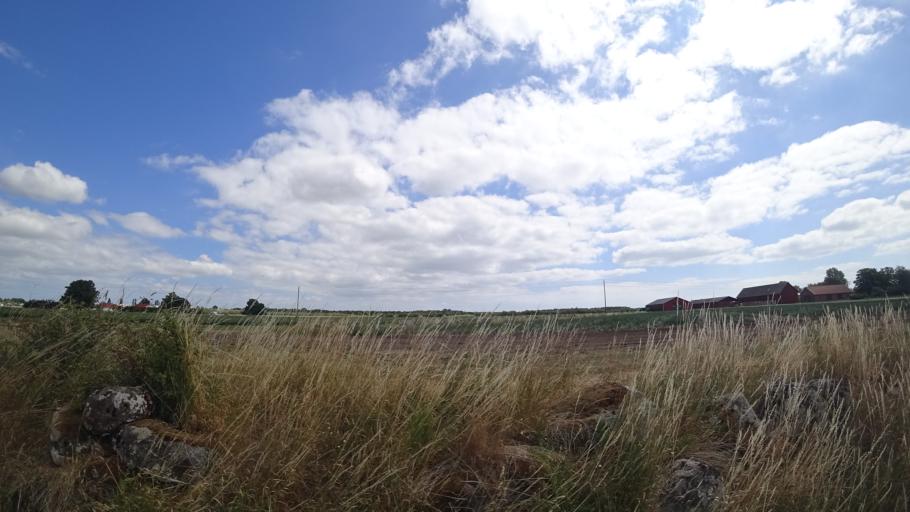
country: SE
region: Skane
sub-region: Kristianstads Kommun
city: Ahus
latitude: 55.9723
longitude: 14.2634
